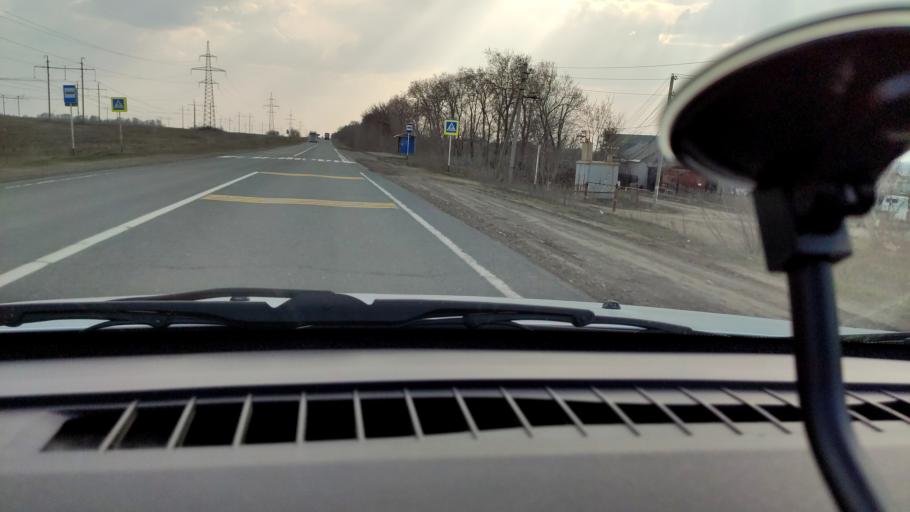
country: RU
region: Samara
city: Dubovyy Umet
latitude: 53.0824
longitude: 50.3910
